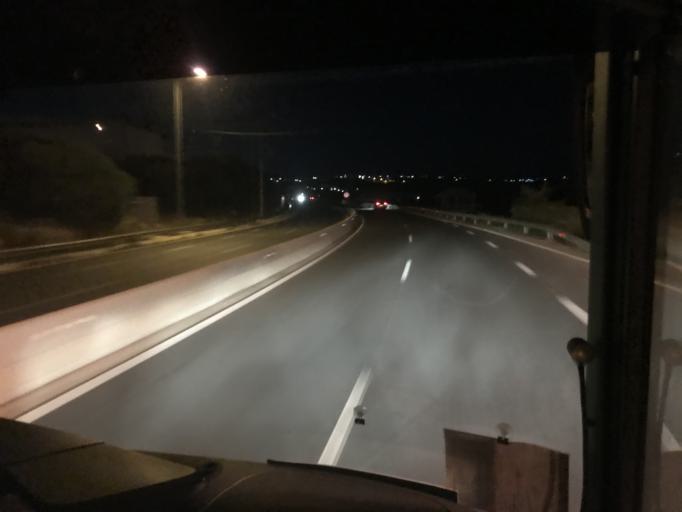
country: GR
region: Crete
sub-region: Nomos Irakleiou
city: Skalanion
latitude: 35.2663
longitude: 25.1847
